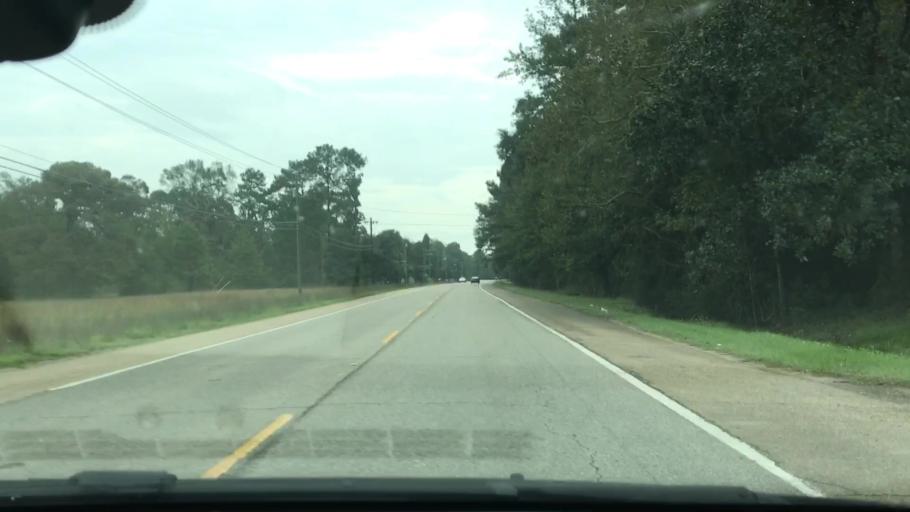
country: US
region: Louisiana
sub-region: Saint Tammany Parish
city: Pearl River
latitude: 30.4062
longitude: -89.7711
